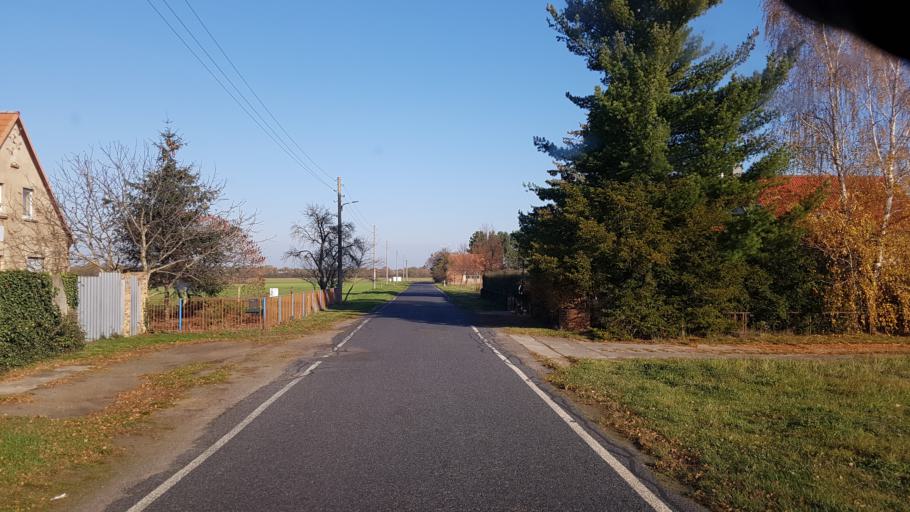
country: DE
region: Brandenburg
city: Grossraschen
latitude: 51.5795
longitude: 13.9411
